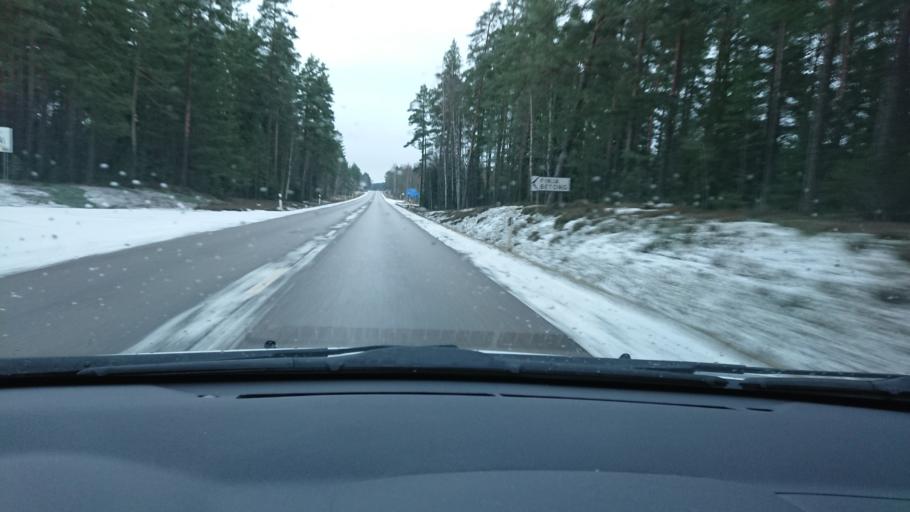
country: SE
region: Kalmar
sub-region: Hultsfreds Kommun
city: Hultsfred
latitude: 57.5315
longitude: 15.8441
